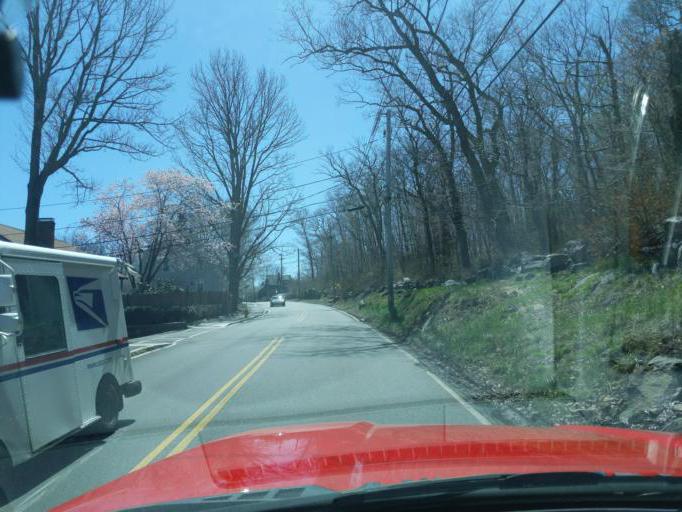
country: US
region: Massachusetts
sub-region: Essex County
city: Rockport
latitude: 42.6604
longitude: -70.6267
